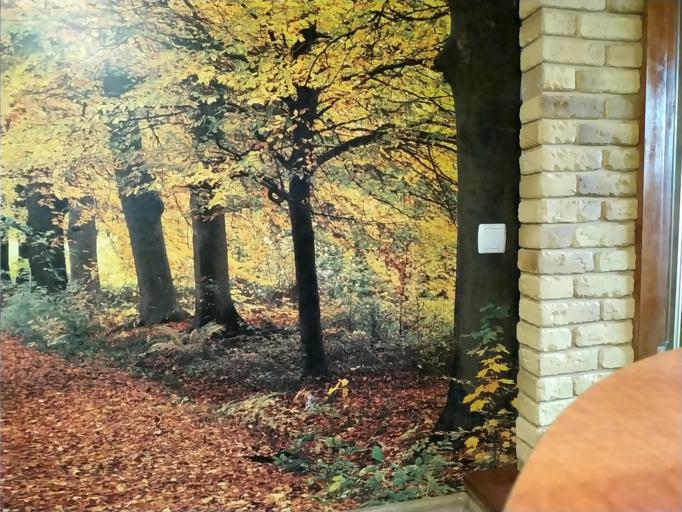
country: RU
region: Leningrad
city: Tolmachevo
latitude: 58.9319
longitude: 29.7119
